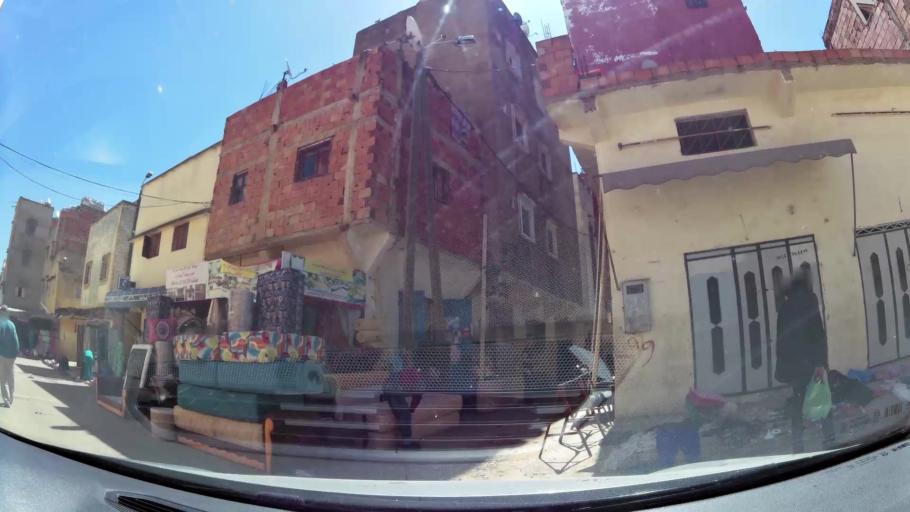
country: MA
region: Meknes-Tafilalet
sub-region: Meknes
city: Meknes
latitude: 33.9071
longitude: -5.5290
